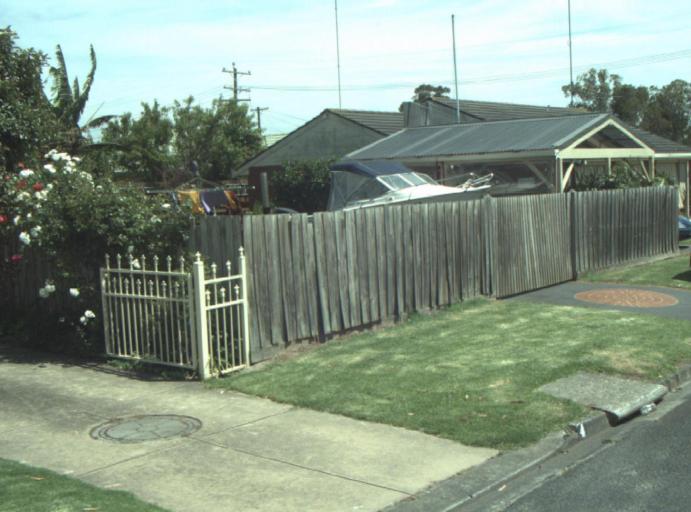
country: AU
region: Victoria
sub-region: Greater Geelong
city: Clifton Springs
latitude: -38.1557
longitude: 144.5766
